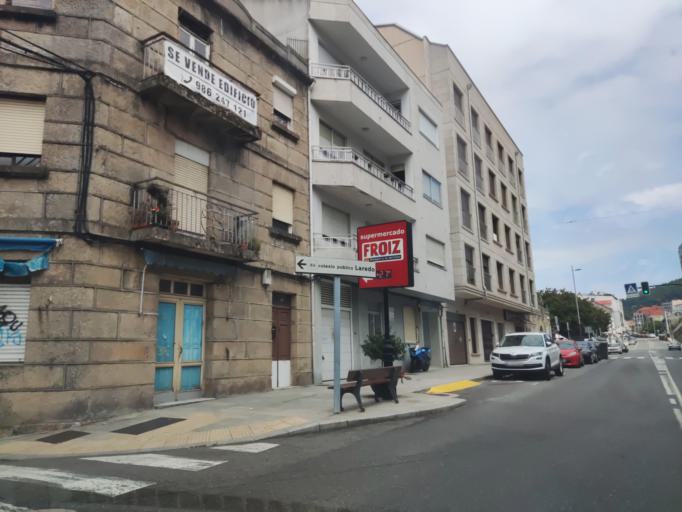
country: ES
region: Galicia
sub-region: Provincia de Pontevedra
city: Vigo
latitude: 42.2673
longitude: -8.6720
